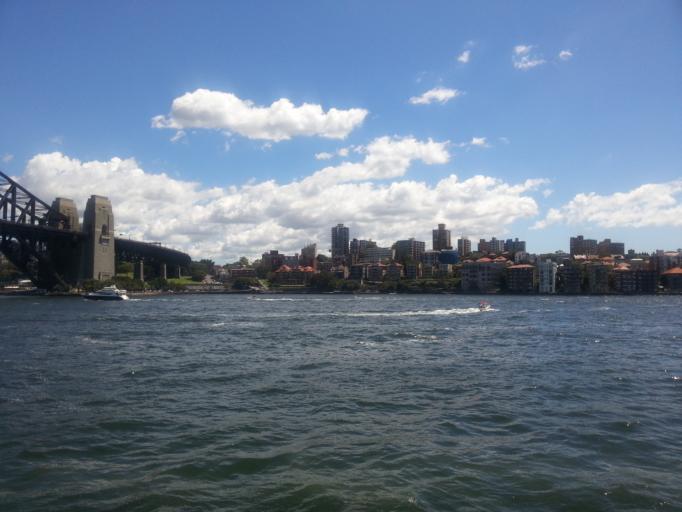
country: AU
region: New South Wales
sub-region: North Sydney
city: Kirribilli
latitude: -33.8548
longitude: 151.2137
